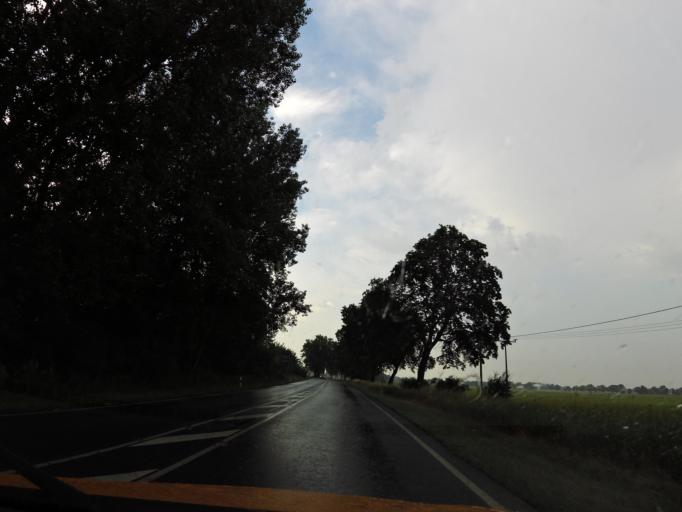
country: DE
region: Brandenburg
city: Friesack
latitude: 52.7498
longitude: 12.5747
